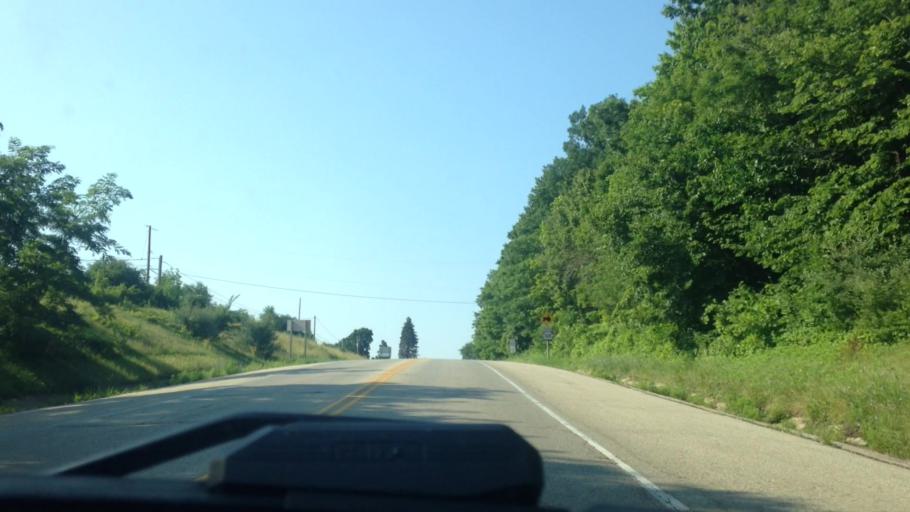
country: US
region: Wisconsin
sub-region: Washington County
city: Richfield
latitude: 43.2509
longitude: -88.2618
